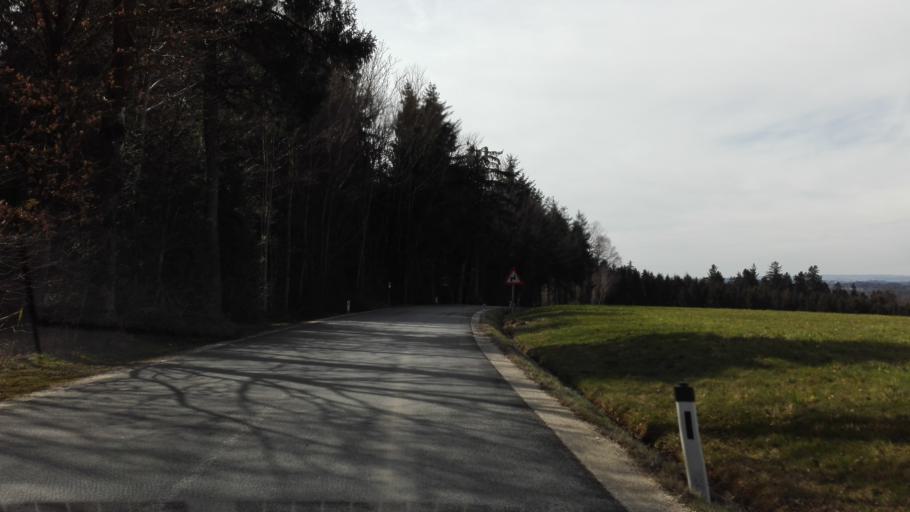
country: AT
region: Upper Austria
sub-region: Politischer Bezirk Scharding
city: Sankt Marienkirchen bei Schaerding
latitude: 48.3702
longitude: 13.6052
